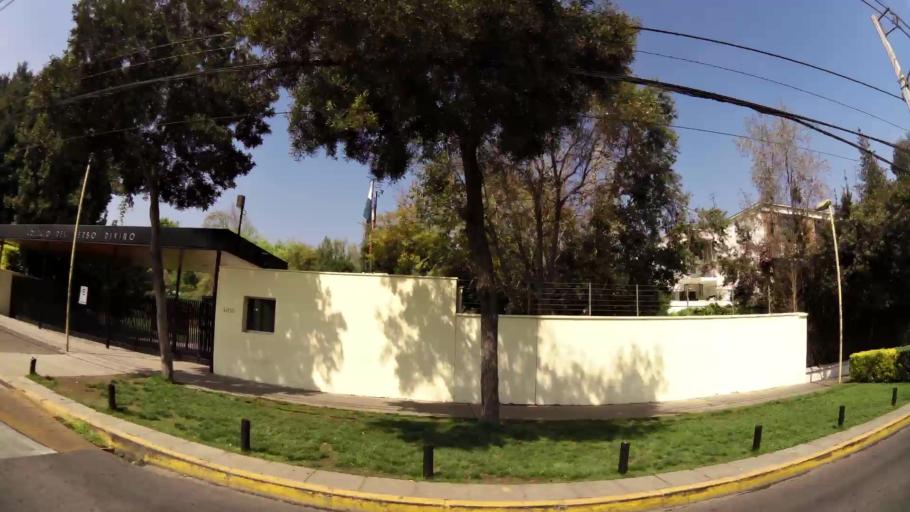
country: CL
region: Santiago Metropolitan
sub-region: Provincia de Santiago
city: Villa Presidente Frei, Nunoa, Santiago, Chile
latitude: -33.4201
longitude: -70.5871
